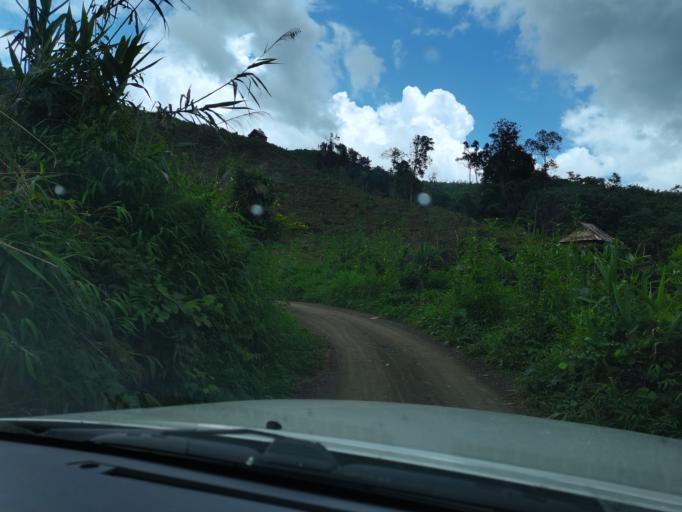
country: LA
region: Loungnamtha
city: Muang Long
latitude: 20.7613
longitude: 101.0172
